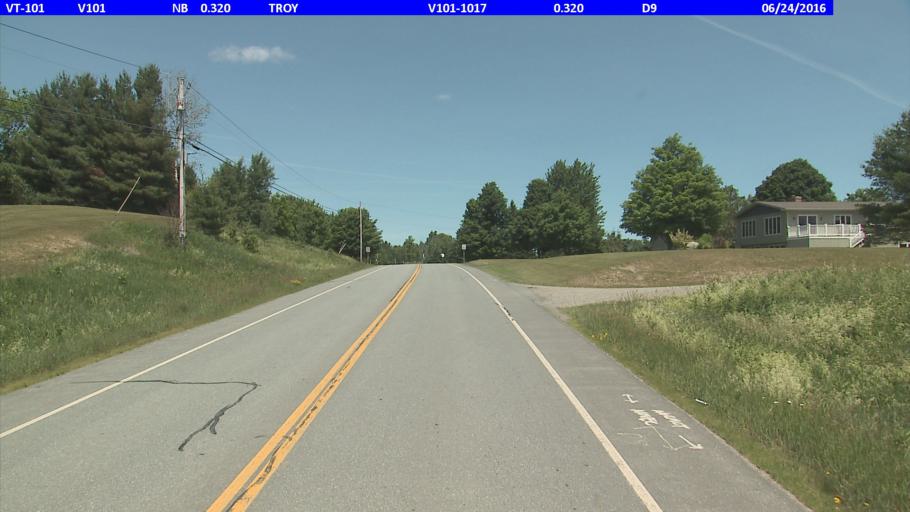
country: US
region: Vermont
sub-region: Orleans County
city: Newport
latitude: 44.9082
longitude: -72.4050
